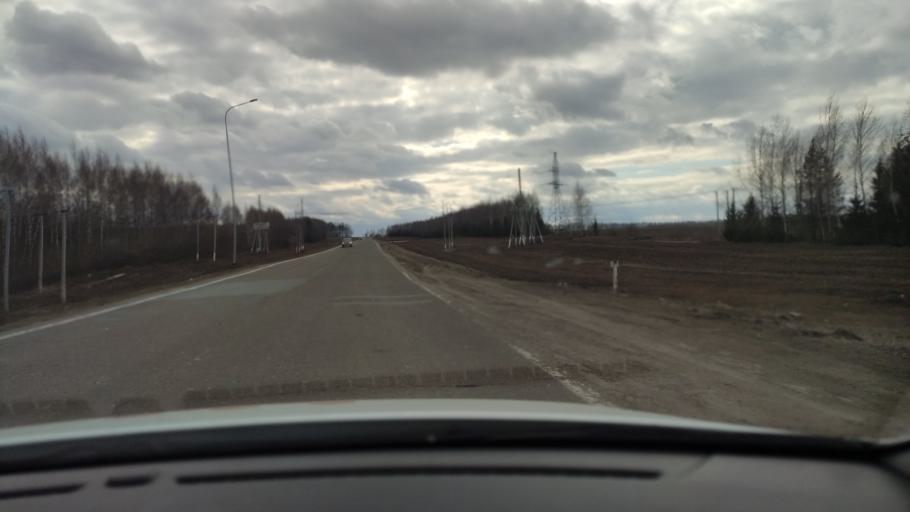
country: RU
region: Tatarstan
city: Vysokaya Gora
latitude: 56.1108
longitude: 49.1823
